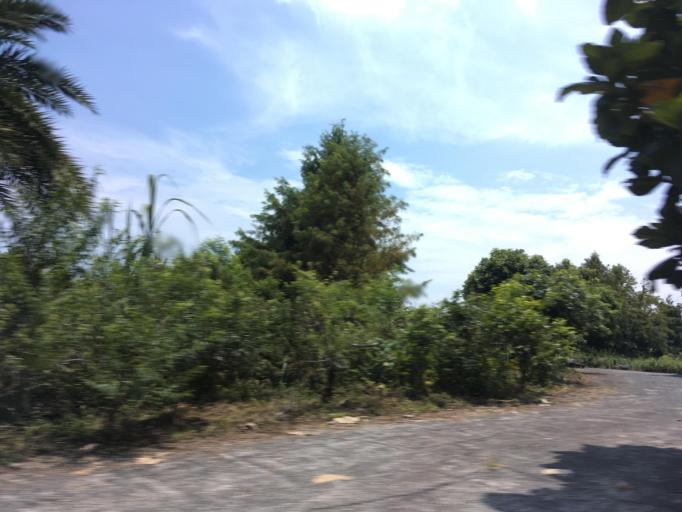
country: TW
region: Taiwan
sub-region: Yilan
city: Yilan
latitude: 24.8197
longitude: 121.7518
